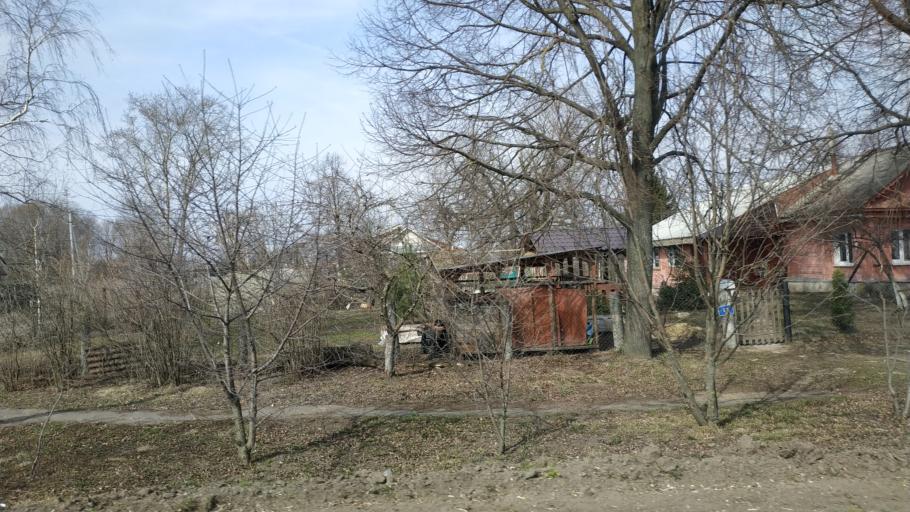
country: RU
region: Moskovskaya
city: Troitskoye
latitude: 55.3562
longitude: 38.5041
